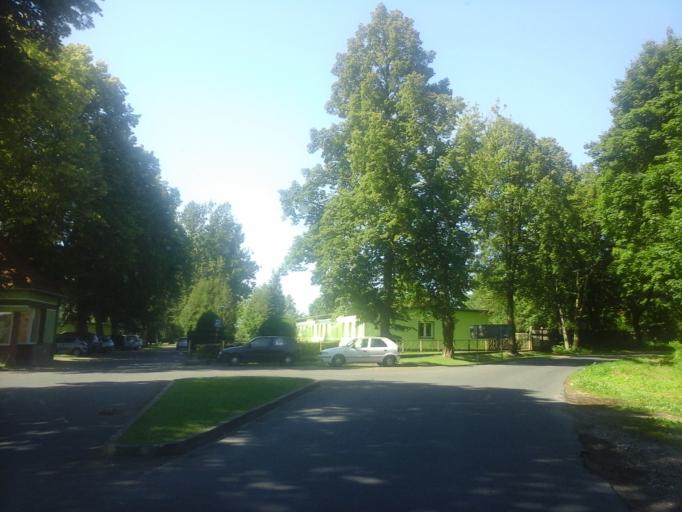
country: PL
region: West Pomeranian Voivodeship
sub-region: Powiat bialogardzki
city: Bialogard
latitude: 54.0181
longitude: 15.9451
